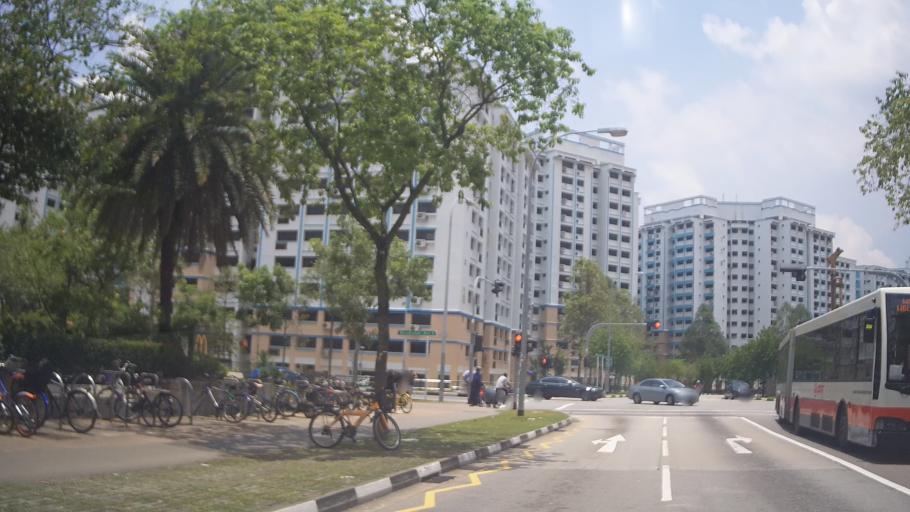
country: MY
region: Johor
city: Johor Bahru
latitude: 1.4456
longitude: 103.7988
